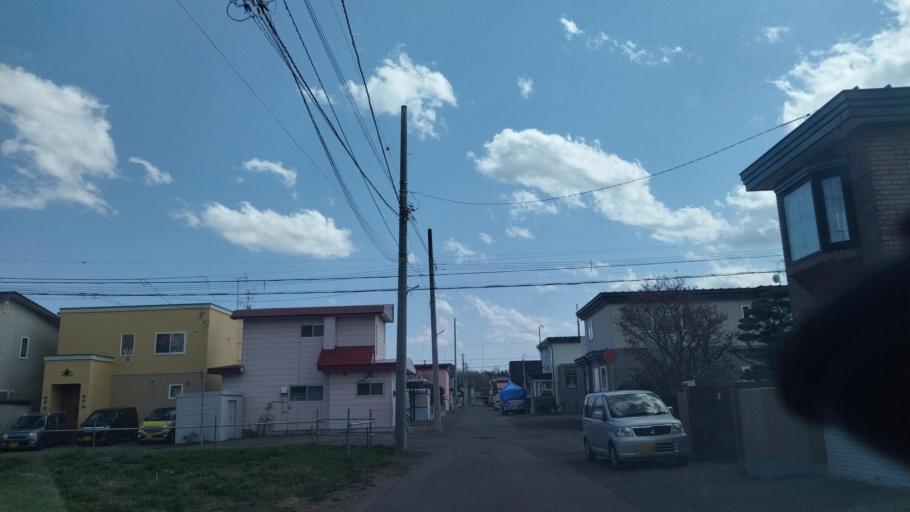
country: JP
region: Hokkaido
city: Obihiro
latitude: 42.9080
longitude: 143.1574
